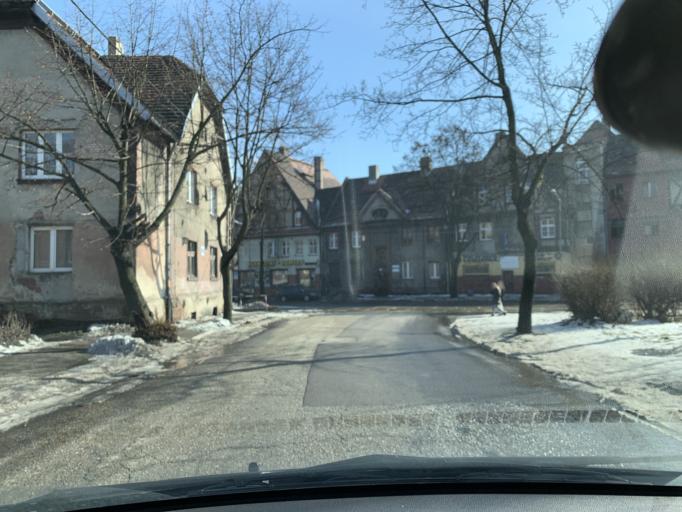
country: PL
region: Silesian Voivodeship
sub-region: Swietochlowice
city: Swietochlowice
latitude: 50.3385
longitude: 18.8707
